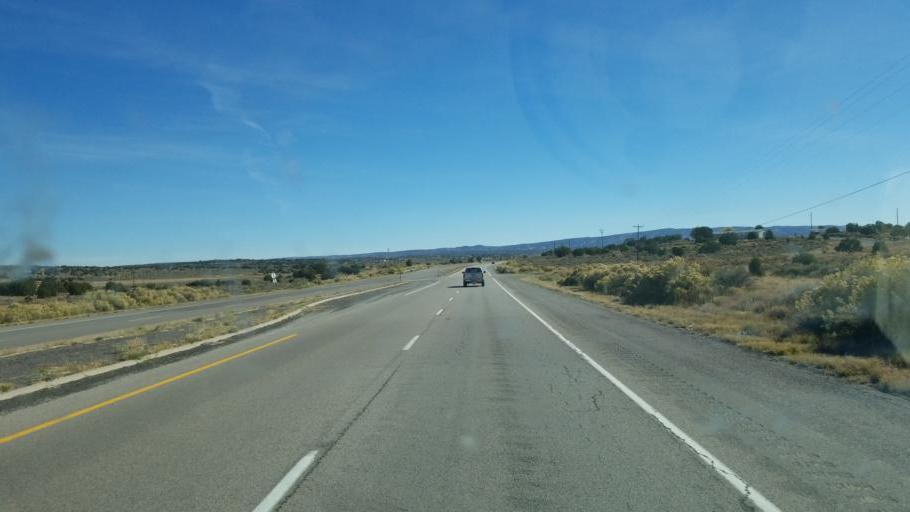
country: US
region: New Mexico
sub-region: McKinley County
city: Twin Lakes
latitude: 35.6361
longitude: -108.8424
